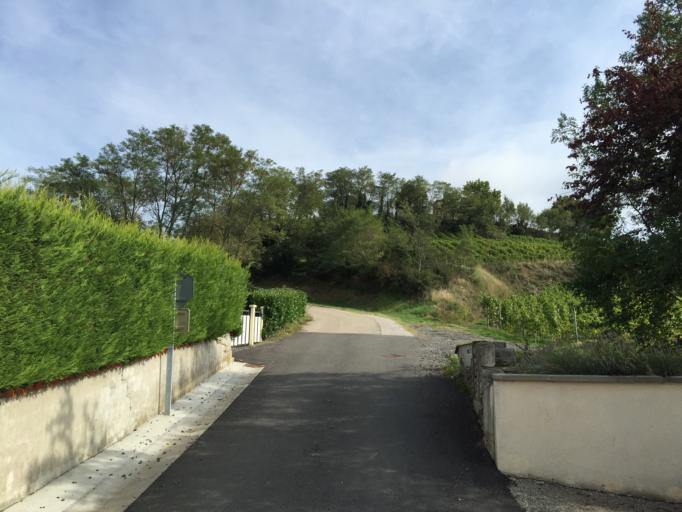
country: FR
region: Rhone-Alpes
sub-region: Departement de la Loire
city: Saint-Romain-le-Puy
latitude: 45.5561
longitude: 4.1237
